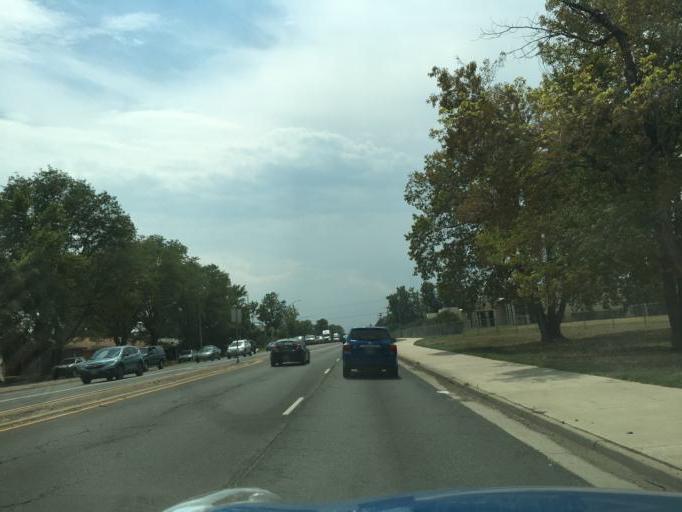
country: US
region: Colorado
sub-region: Jefferson County
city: Wheat Ridge
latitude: 39.7618
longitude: -105.0816
